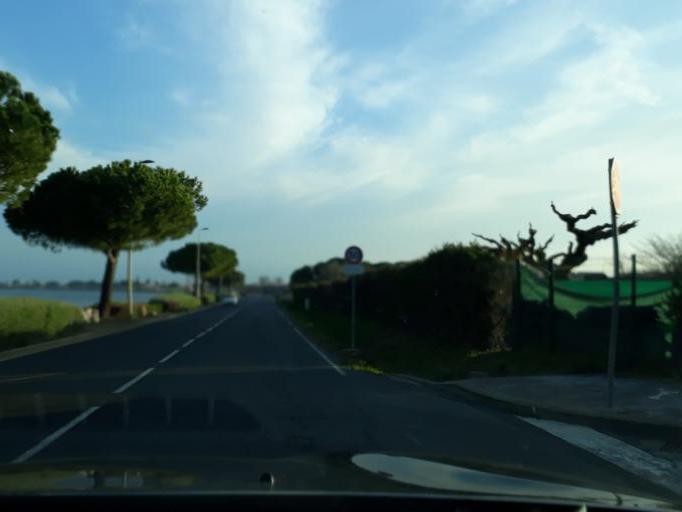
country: FR
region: Languedoc-Roussillon
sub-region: Departement de l'Herault
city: Marseillan
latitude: 43.3477
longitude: 3.5311
